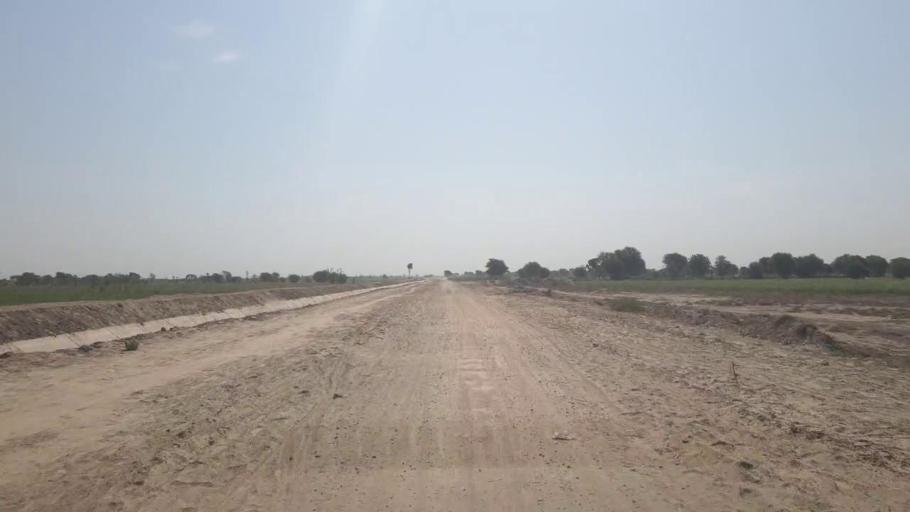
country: PK
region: Sindh
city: Kunri
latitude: 25.2719
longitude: 69.6251
